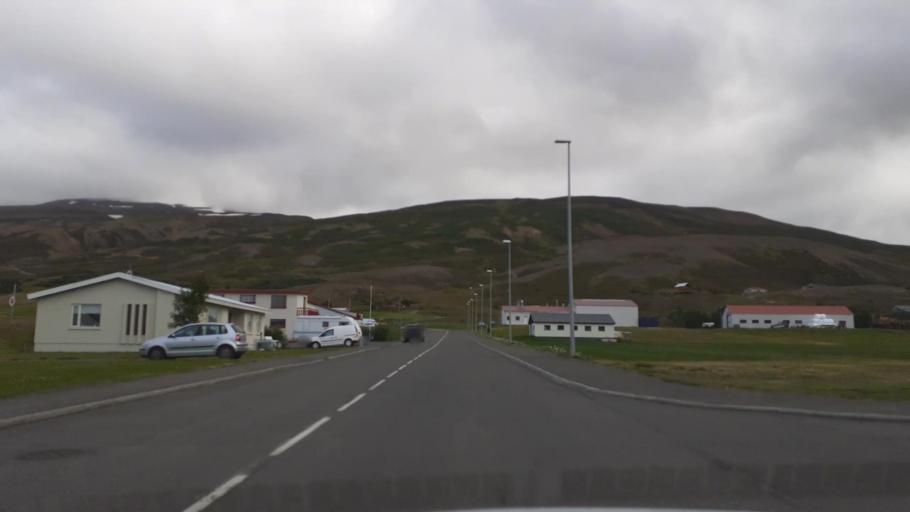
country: IS
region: Northeast
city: Akureyri
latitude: 65.9504
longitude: -18.1801
